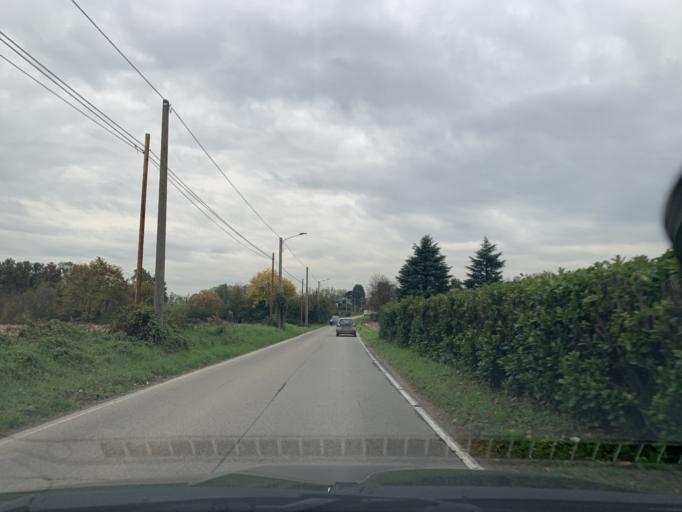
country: IT
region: Lombardy
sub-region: Provincia di Como
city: Bulgorello
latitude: 45.7193
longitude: 9.0528
